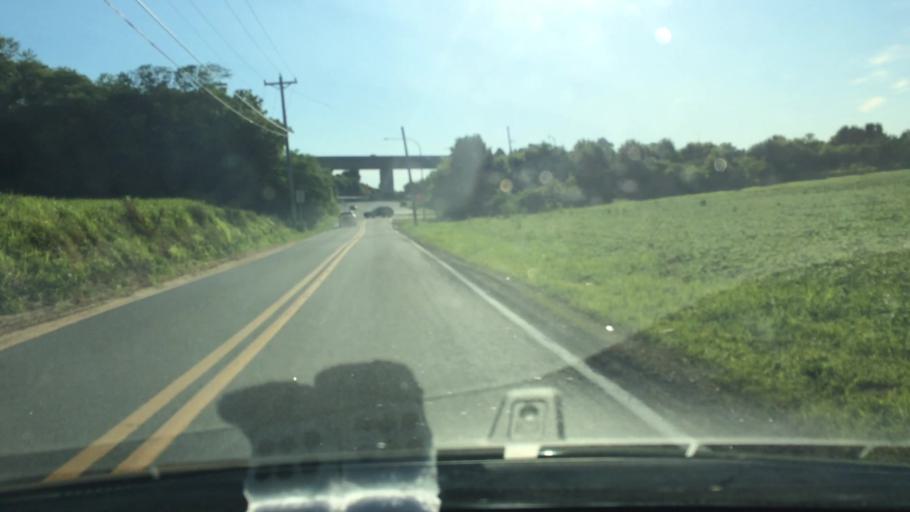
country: US
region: Delaware
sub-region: New Castle County
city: Delaware City
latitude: 39.5438
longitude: -75.6562
